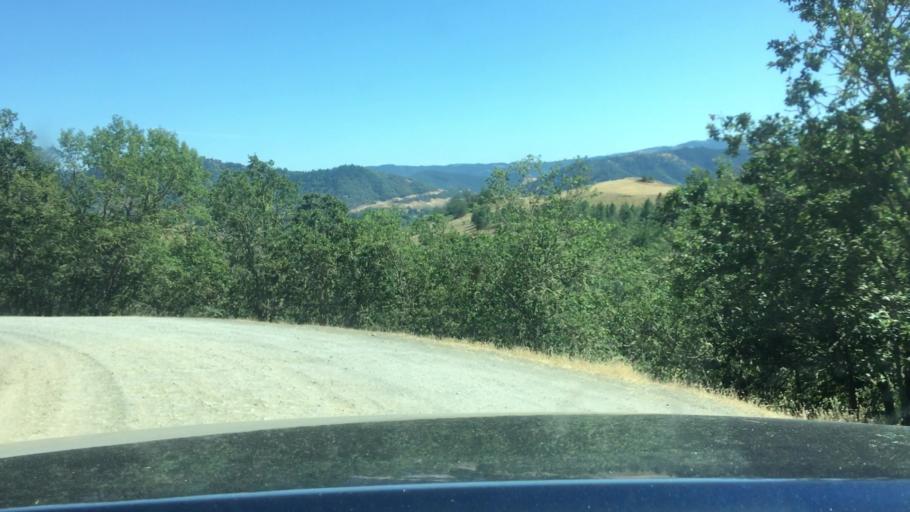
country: US
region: Oregon
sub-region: Douglas County
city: Winston
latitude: 43.1363
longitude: -123.4386
